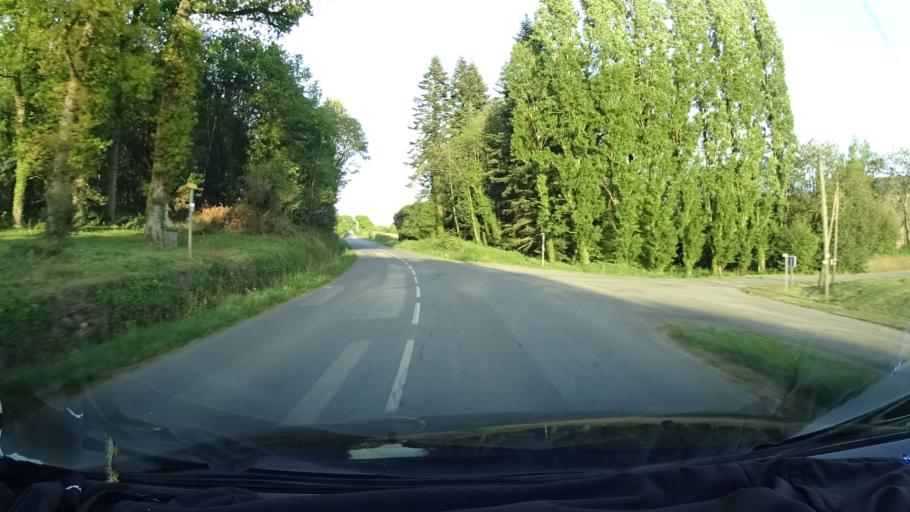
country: FR
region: Brittany
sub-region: Departement du Morbihan
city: Peaule
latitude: 47.5851
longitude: -2.3668
